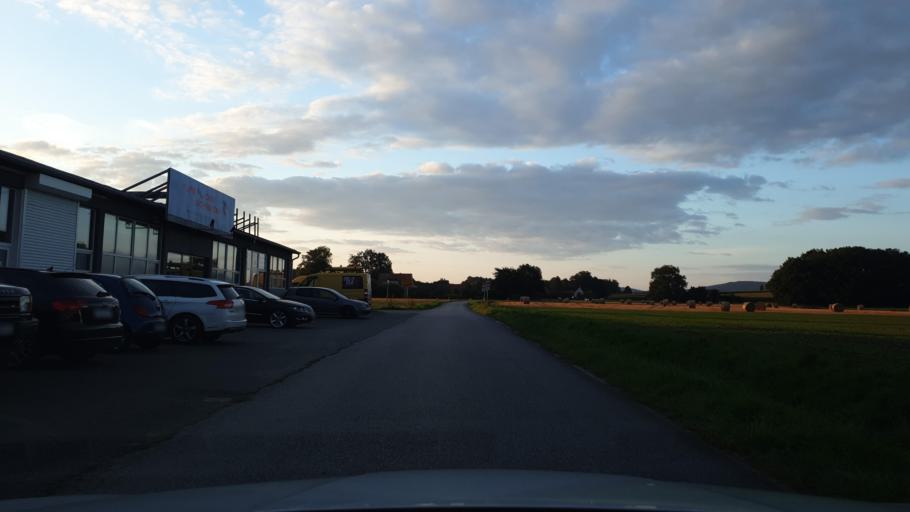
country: DE
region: North Rhine-Westphalia
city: Bad Oeynhausen
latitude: 52.2184
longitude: 8.7529
